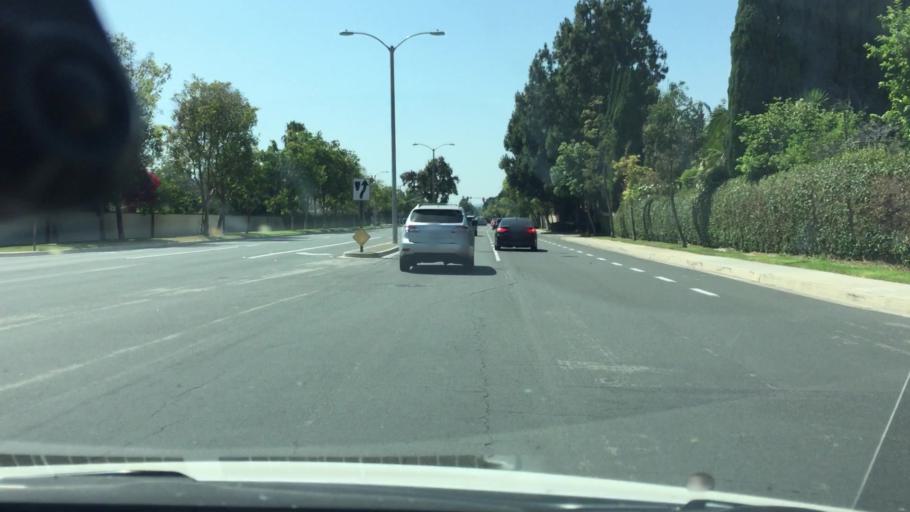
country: US
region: California
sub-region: Orange County
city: North Tustin
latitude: 33.7147
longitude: -117.7745
